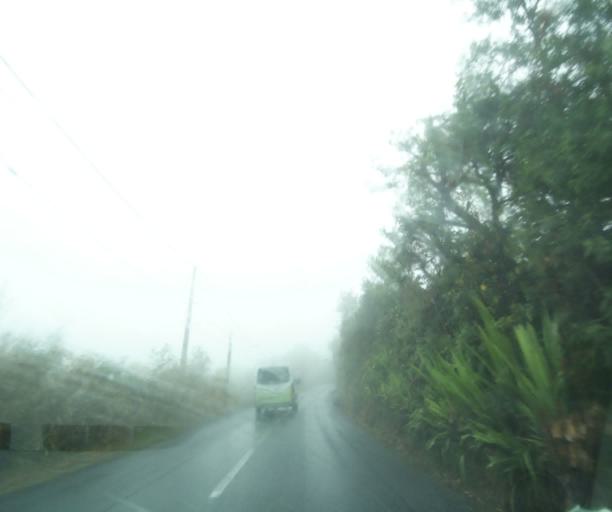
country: RE
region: Reunion
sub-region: Reunion
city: Saint-Paul
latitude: -21.0086
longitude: 55.3170
